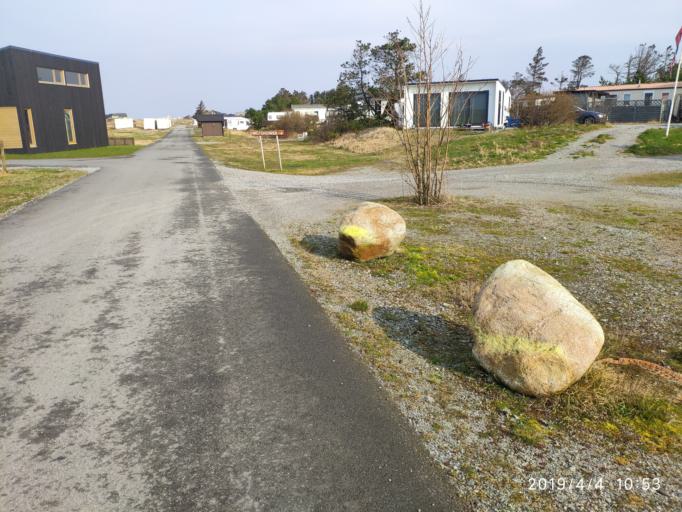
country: NO
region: Rogaland
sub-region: Klepp
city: Kleppe
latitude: 58.8000
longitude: 5.5573
